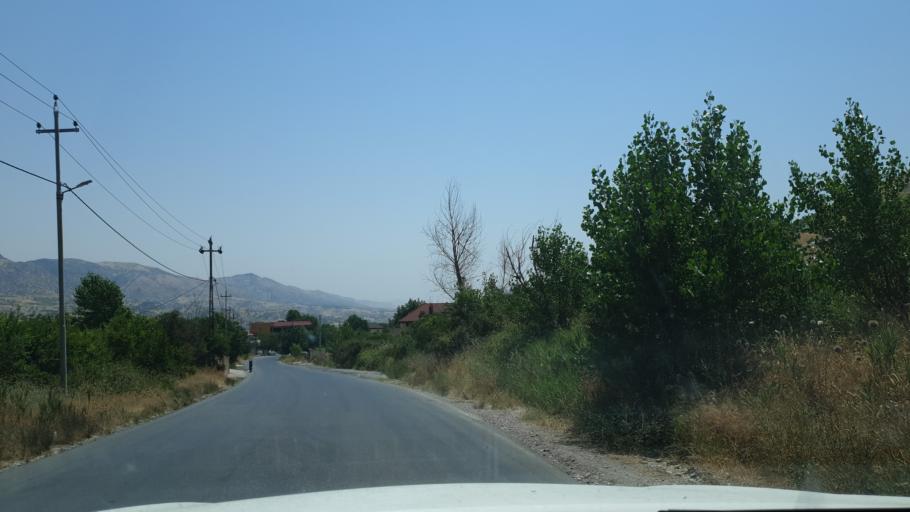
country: IQ
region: Arbil
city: Nahiyat Hiran
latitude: 36.2909
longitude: 44.4791
